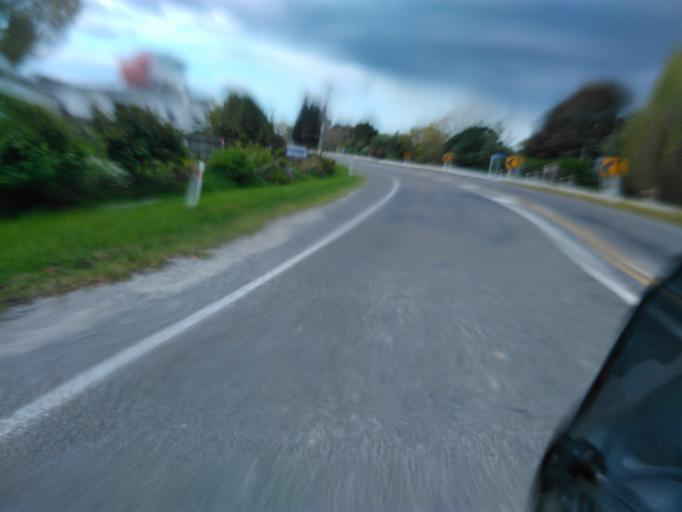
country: NZ
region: Gisborne
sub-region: Gisborne District
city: Gisborne
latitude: -38.6578
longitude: 177.9454
